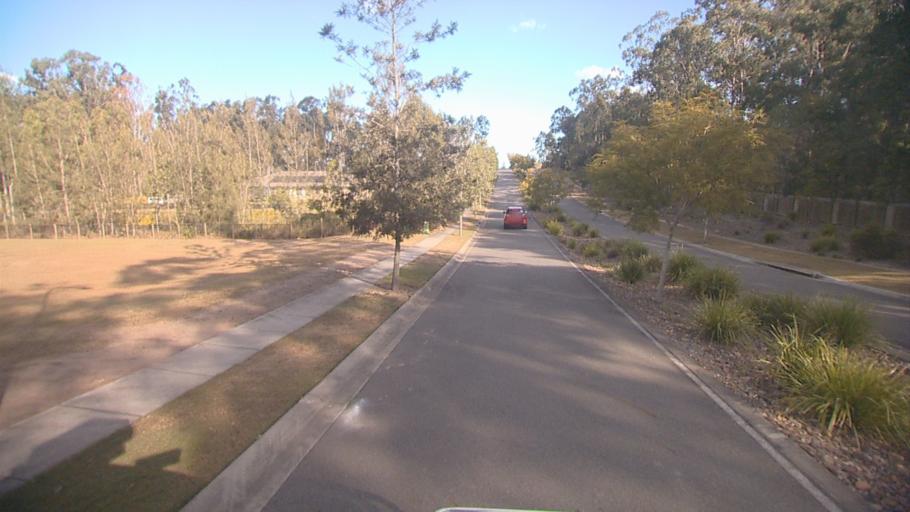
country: AU
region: Queensland
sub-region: Logan
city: North Maclean
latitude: -27.8220
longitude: 152.9804
